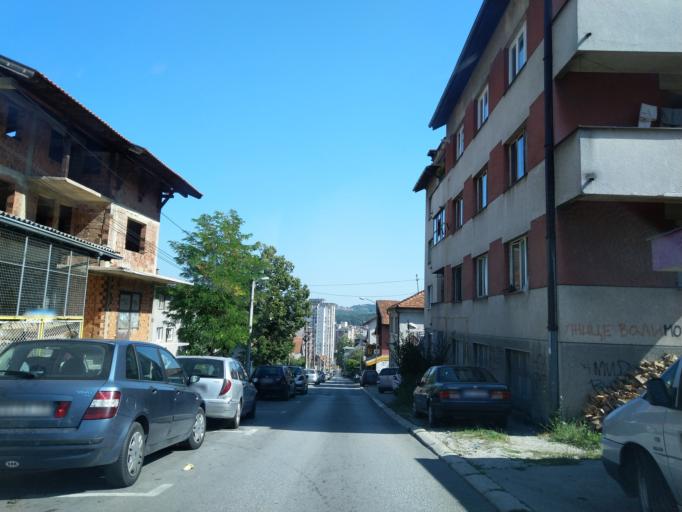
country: RS
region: Central Serbia
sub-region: Zlatiborski Okrug
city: Uzice
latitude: 43.8574
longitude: 19.8293
